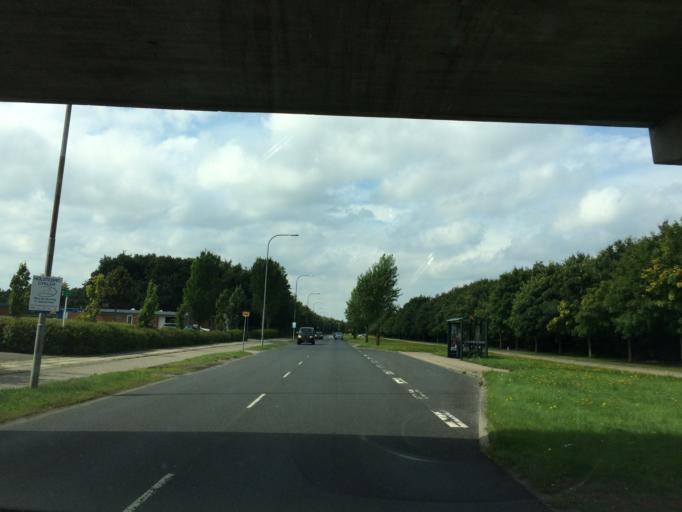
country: DK
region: Central Jutland
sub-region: Holstebro Kommune
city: Holstebro
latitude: 56.3747
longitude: 8.6065
